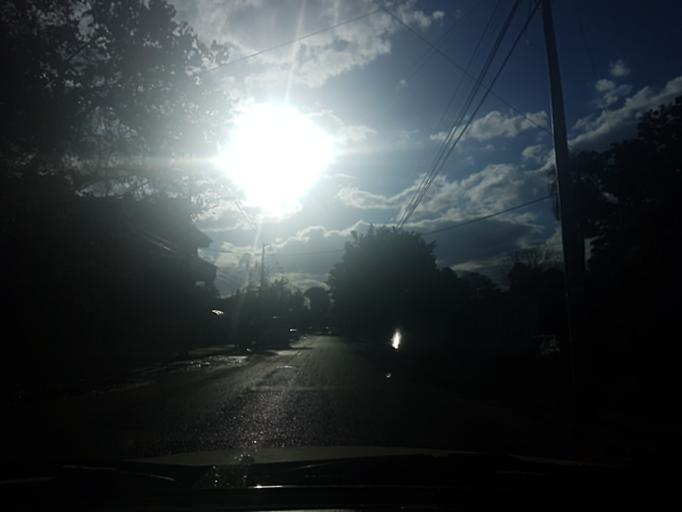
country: PY
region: Asuncion
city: Asuncion
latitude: -25.2691
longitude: -57.5787
